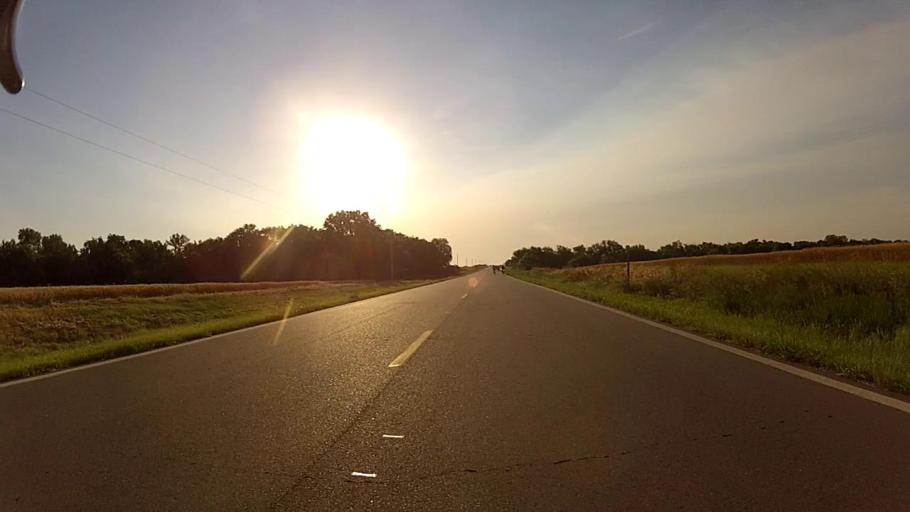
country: US
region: Kansas
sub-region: Harper County
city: Anthony
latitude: 37.1541
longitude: -97.8402
